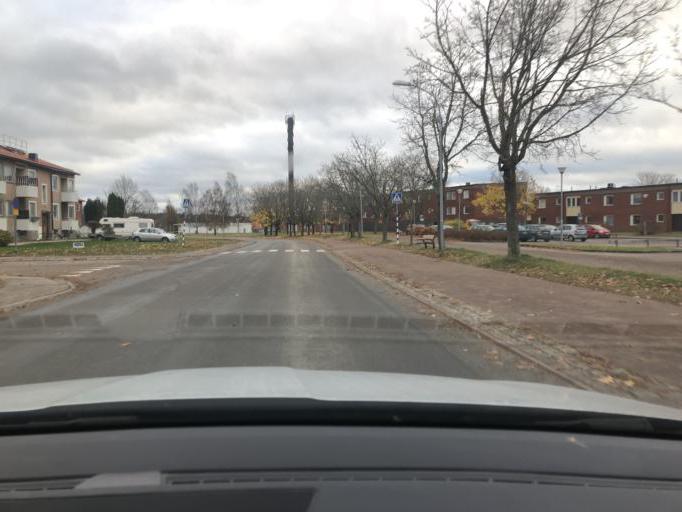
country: SE
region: Uppsala
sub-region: Tierps Kommun
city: Tierp
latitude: 60.3407
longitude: 17.5138
